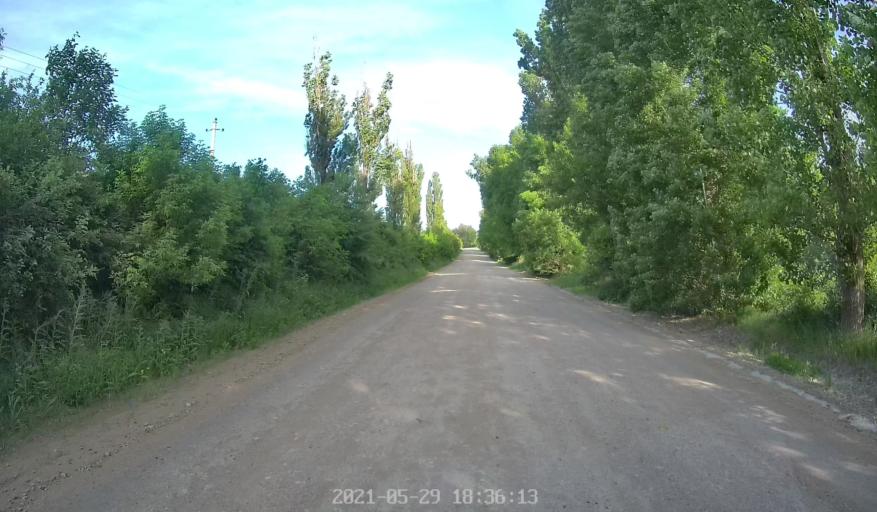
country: MD
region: Chisinau
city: Singera
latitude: 46.8073
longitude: 28.9234
